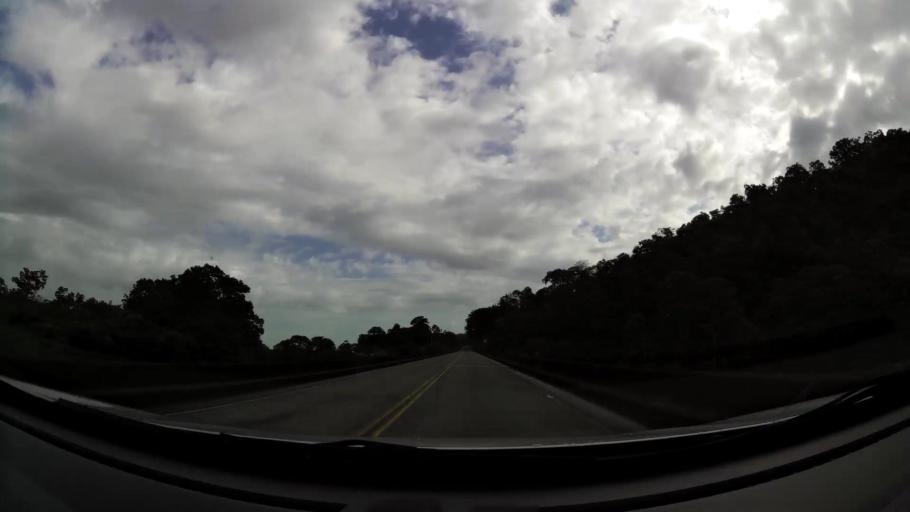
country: CR
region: Limon
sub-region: Canton de Siquirres
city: Siquirres
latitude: 10.0926
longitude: -83.4874
